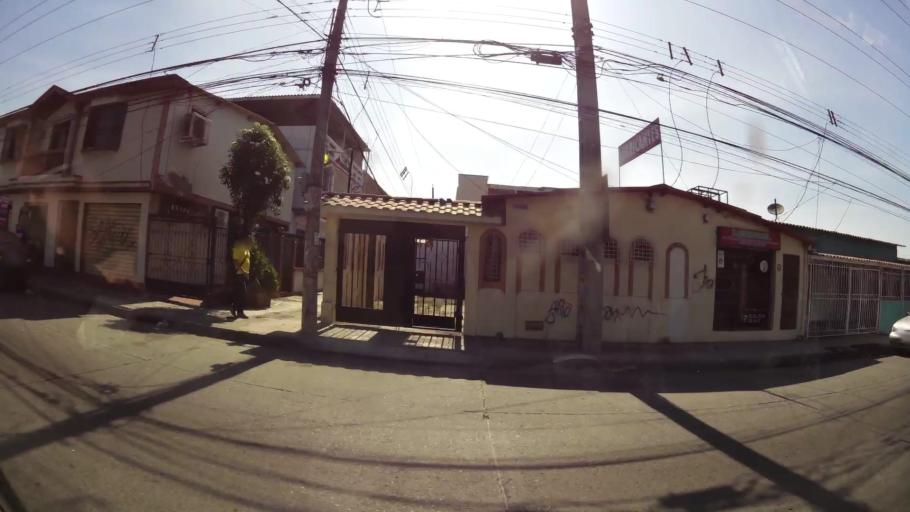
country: EC
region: Guayas
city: Eloy Alfaro
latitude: -2.1435
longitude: -79.9021
